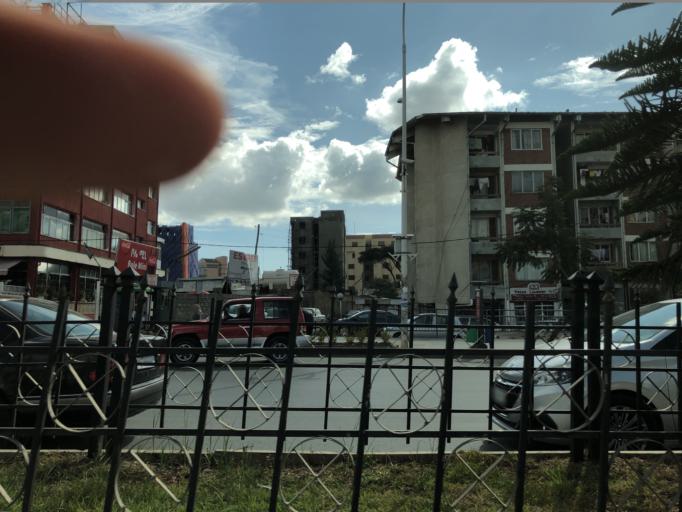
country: ET
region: Adis Abeba
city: Addis Ababa
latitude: 8.9891
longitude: 38.7885
